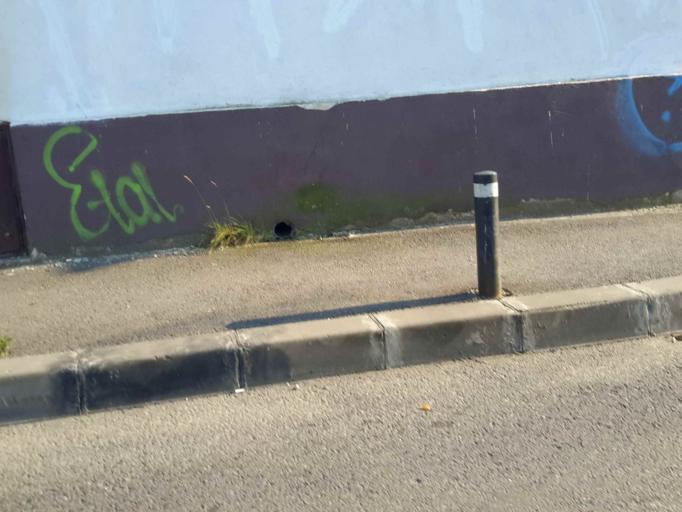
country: RO
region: Cluj
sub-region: Municipiul Cluj-Napoca
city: Cluj-Napoca
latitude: 46.7733
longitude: 23.5938
